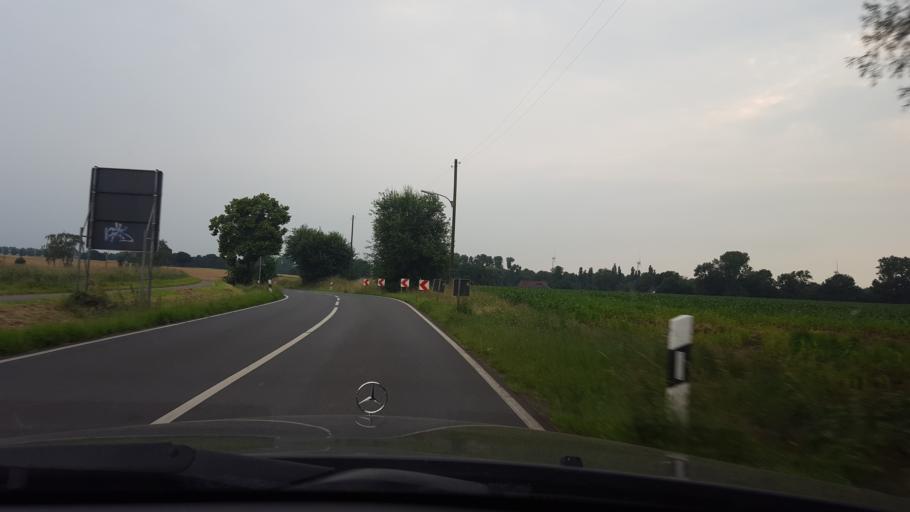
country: DE
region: North Rhine-Westphalia
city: Oer-Erkenschwick
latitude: 51.6446
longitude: 7.2391
